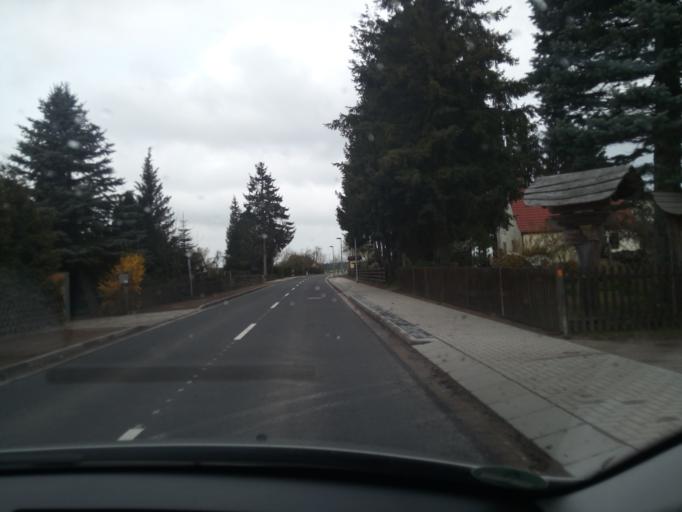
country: DE
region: Brandenburg
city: Lychen
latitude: 53.2927
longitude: 13.3366
